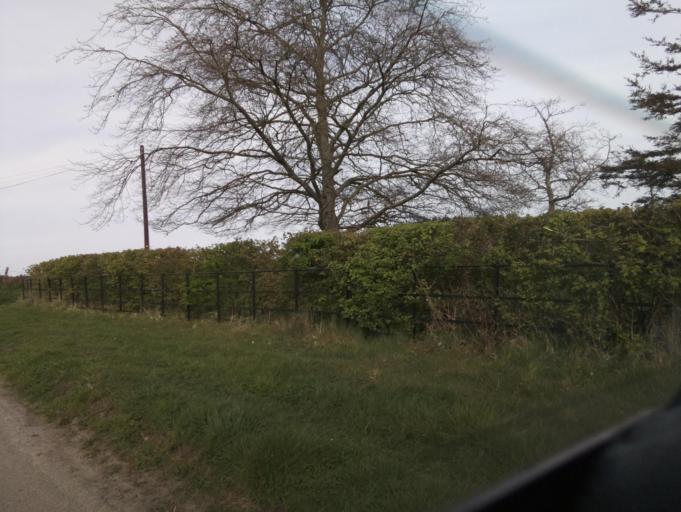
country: GB
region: England
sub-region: Somerset
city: Milborne Port
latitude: 50.9409
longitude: -2.4710
